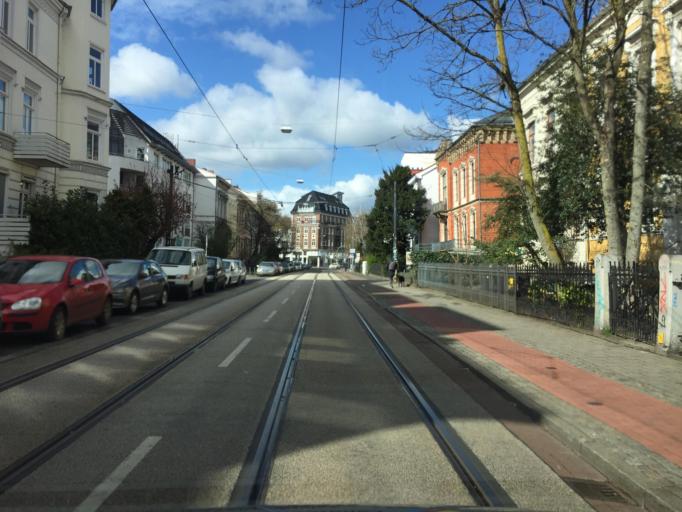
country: DE
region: Bremen
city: Bremen
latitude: 53.0738
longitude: 8.8229
